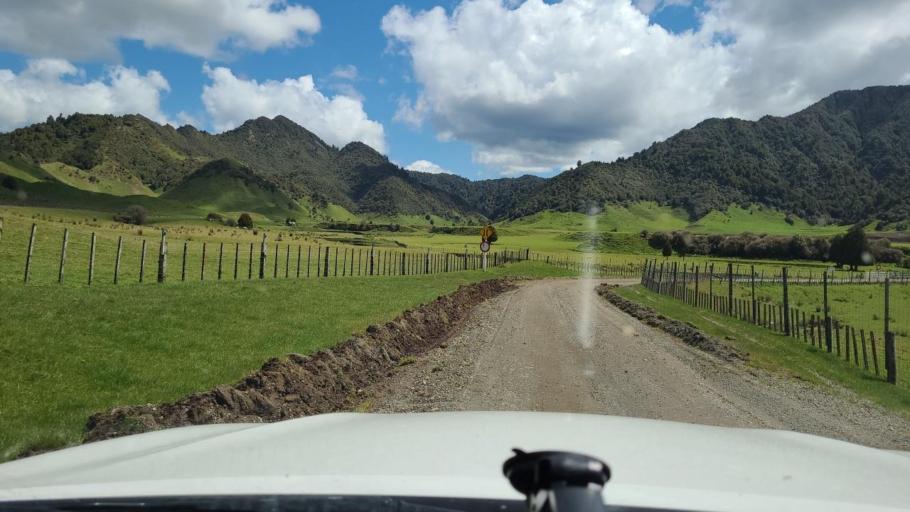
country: NZ
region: Bay of Plenty
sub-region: Opotiki District
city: Opotiki
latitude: -38.2801
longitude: 177.5131
